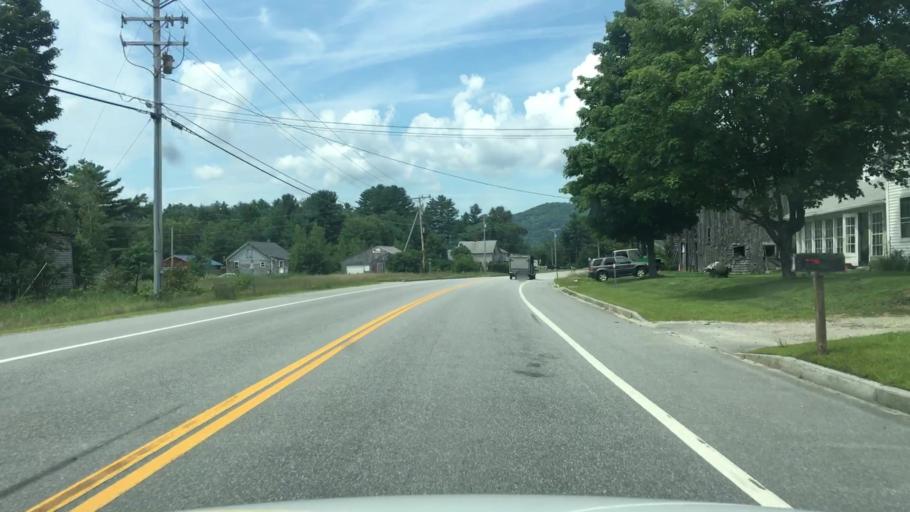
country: US
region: New Hampshire
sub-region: Grafton County
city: Rumney
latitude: 43.8206
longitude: -71.8877
